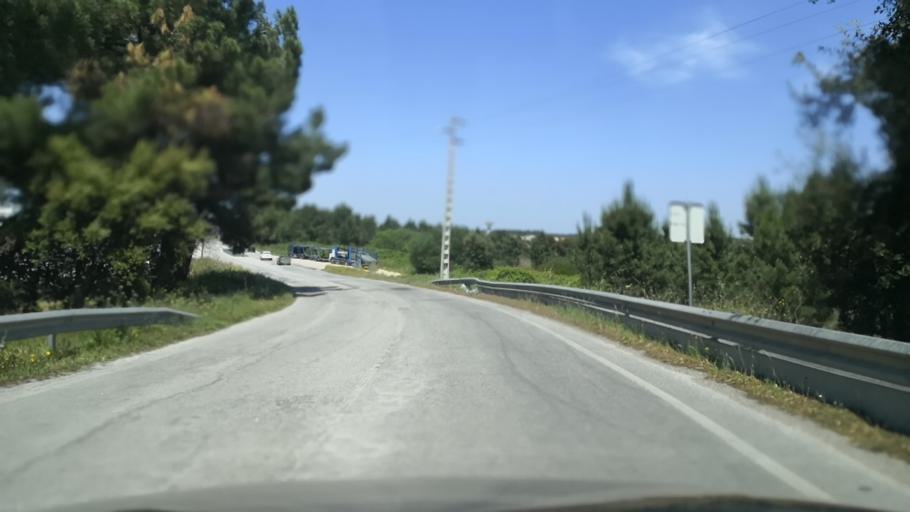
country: PT
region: Setubal
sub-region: Palmela
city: Palmela
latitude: 38.6209
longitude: -8.7466
